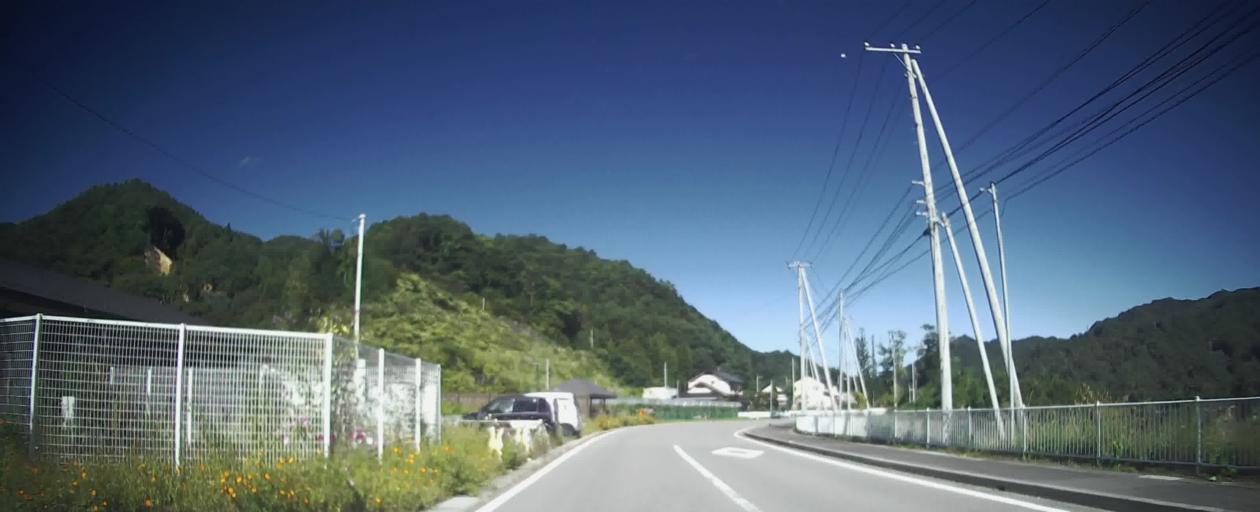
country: JP
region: Gunma
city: Nakanojomachi
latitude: 36.5563
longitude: 138.7036
